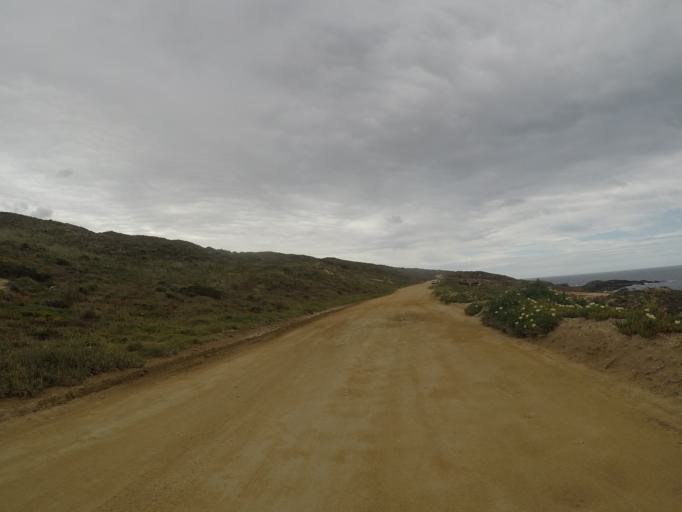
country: PT
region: Beja
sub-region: Odemira
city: Vila Nova de Milfontes
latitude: 37.6422
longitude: -8.8064
